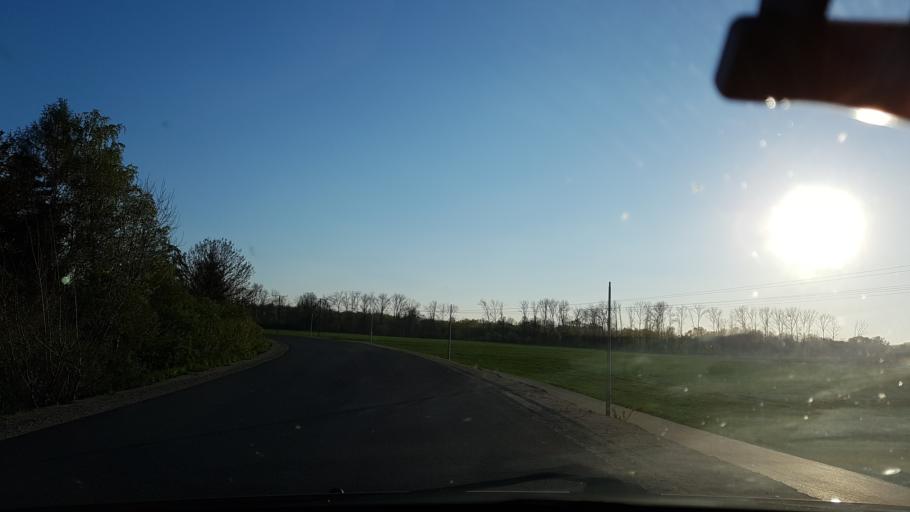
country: PL
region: Opole Voivodeship
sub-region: Powiat nyski
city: Nysa
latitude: 50.4389
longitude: 17.3059
